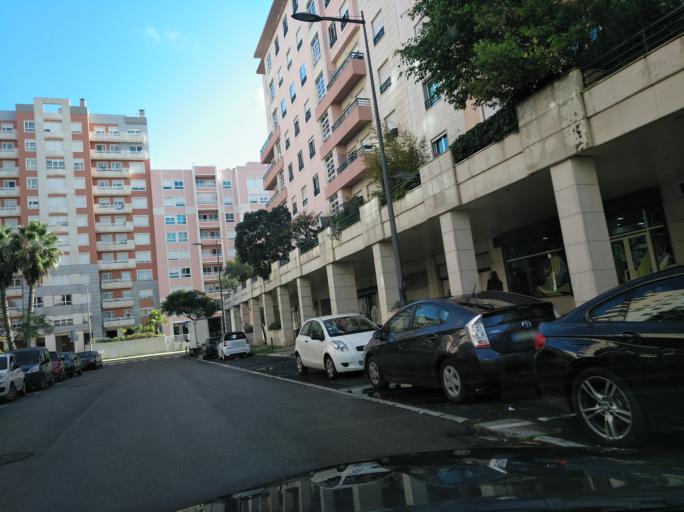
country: PT
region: Lisbon
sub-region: Odivelas
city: Pontinha
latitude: 38.7621
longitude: -9.1746
